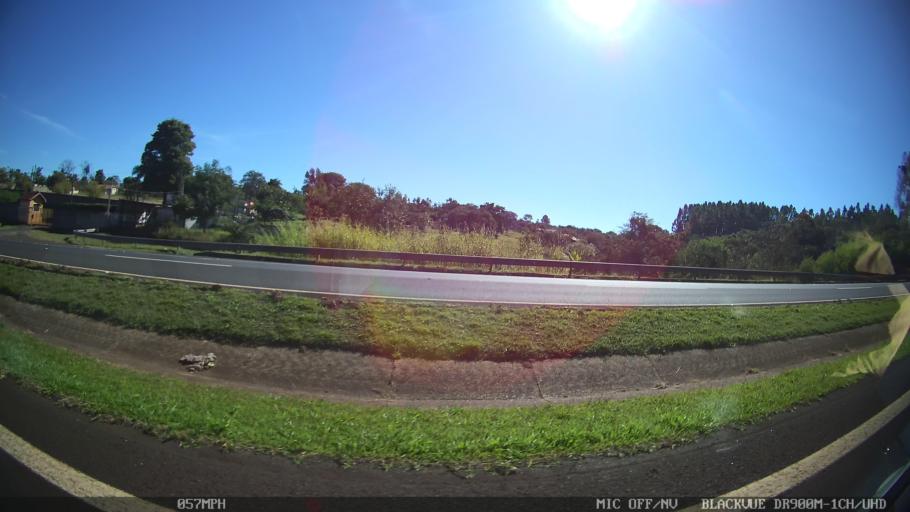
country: BR
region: Sao Paulo
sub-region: Franca
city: Franca
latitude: -20.5768
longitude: -47.3529
